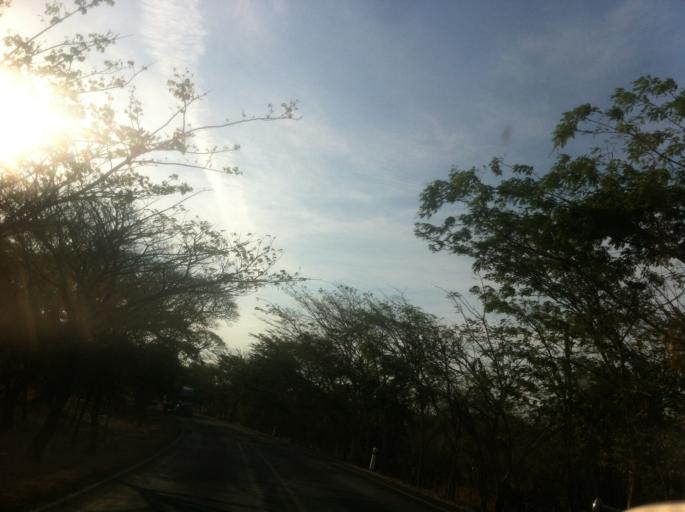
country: NI
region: Rivas
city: Cardenas
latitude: 11.2722
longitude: -85.6514
